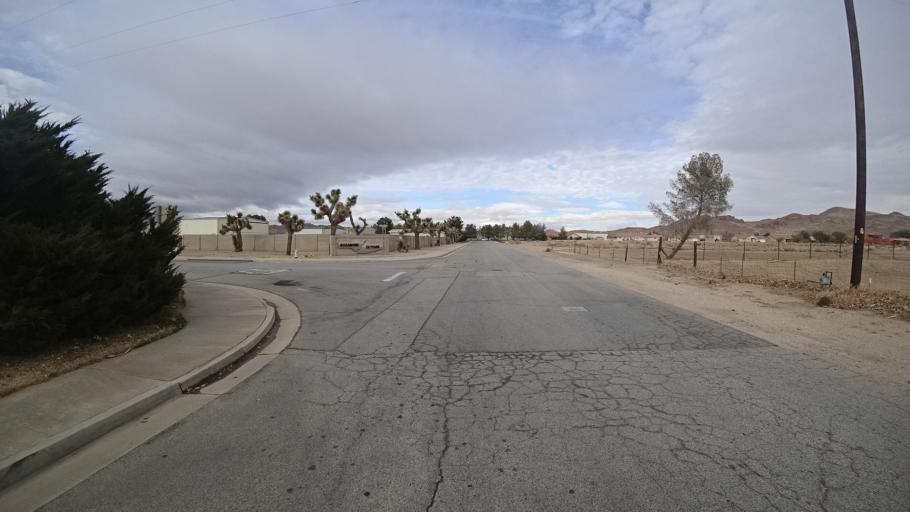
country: US
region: California
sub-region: Kern County
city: Rosamond
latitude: 34.8673
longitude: -118.2026
